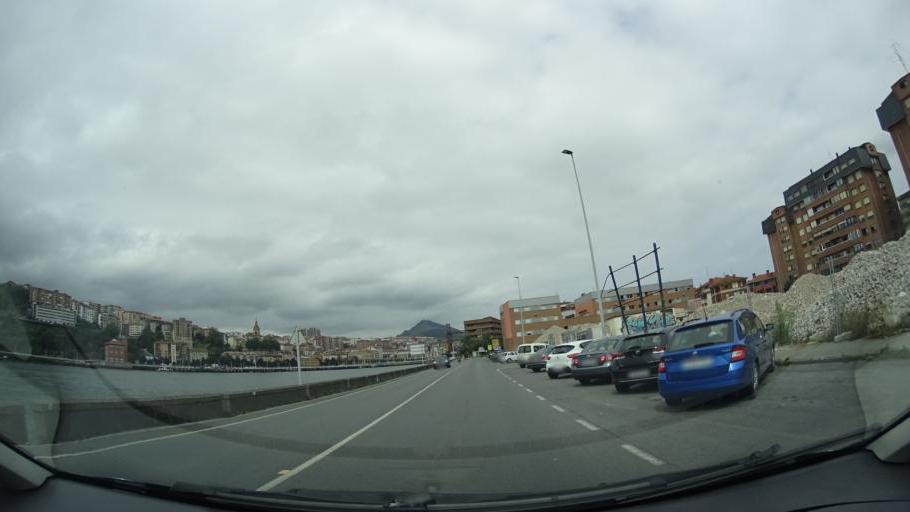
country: ES
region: Basque Country
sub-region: Bizkaia
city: Sestao
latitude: 43.3202
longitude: -3.0097
